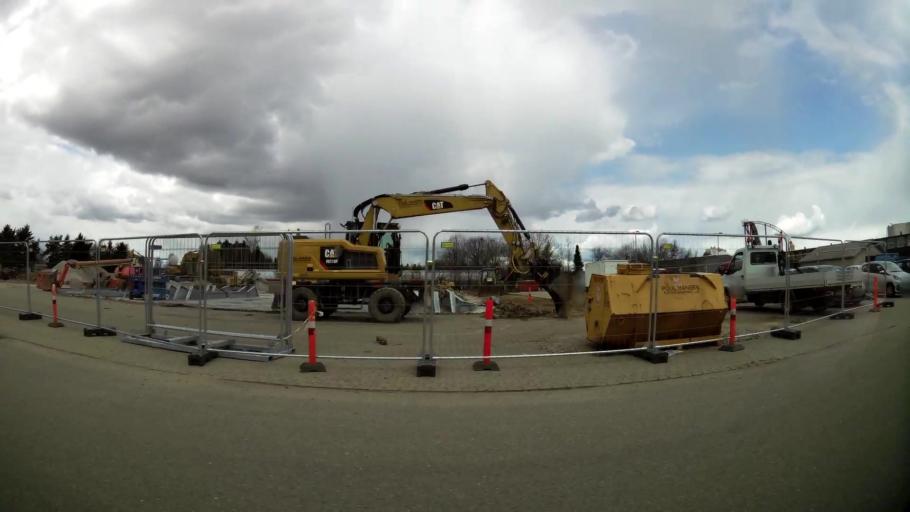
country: DK
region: South Denmark
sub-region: Billund Kommune
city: Billund
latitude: 55.7353
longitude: 9.1221
